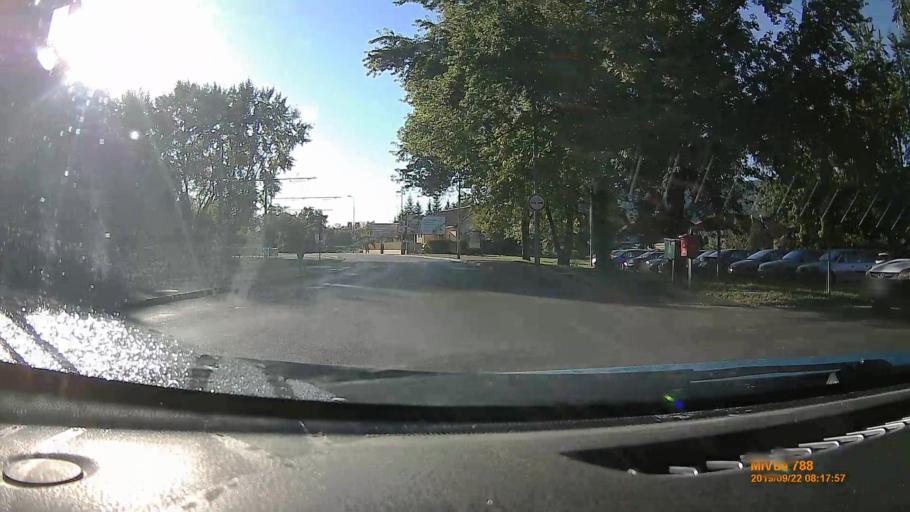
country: HU
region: Borsod-Abauj-Zemplen
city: Sajobabony
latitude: 48.1076
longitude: 20.6768
